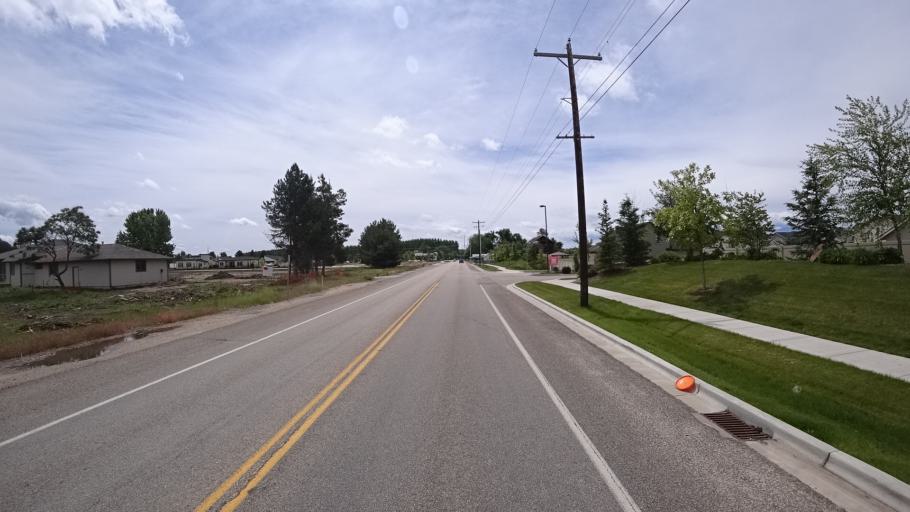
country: US
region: Idaho
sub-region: Ada County
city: Eagle
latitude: 43.6986
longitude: -116.4037
